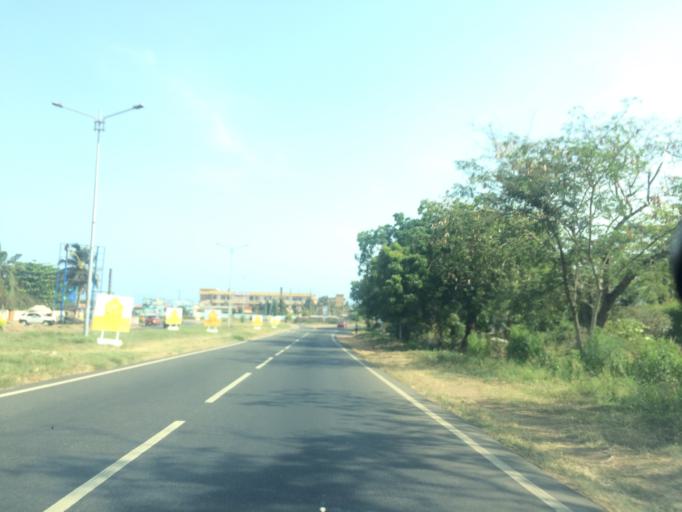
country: GH
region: Greater Accra
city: Accra
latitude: 5.5581
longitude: -0.1679
